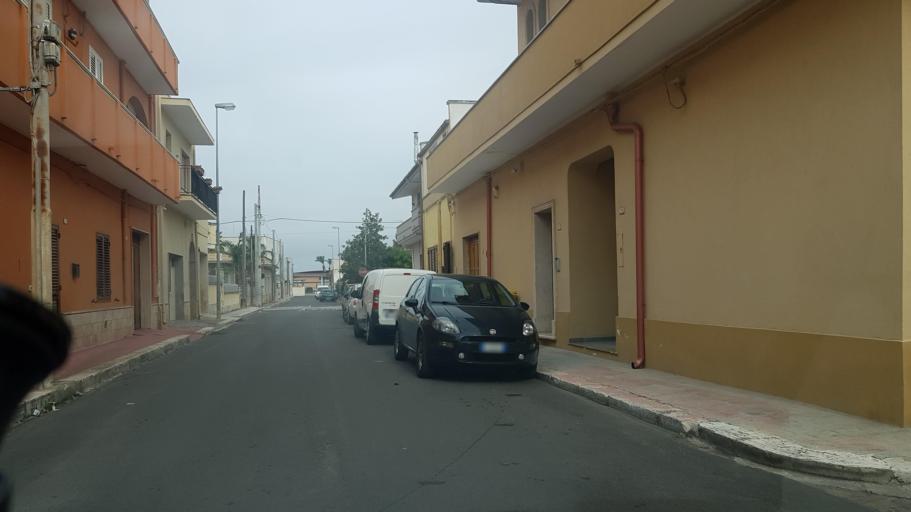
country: IT
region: Apulia
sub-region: Provincia di Brindisi
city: Cellino San Marco
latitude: 40.4751
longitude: 17.9645
